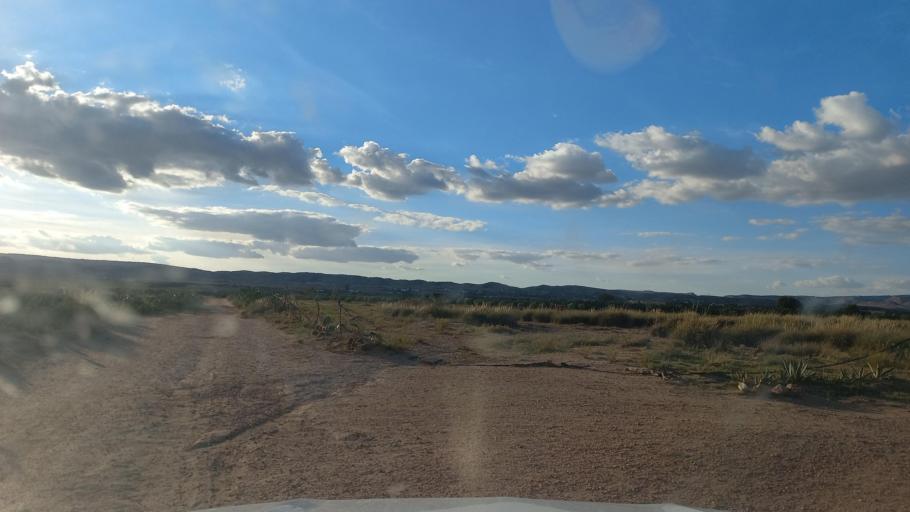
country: TN
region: Al Qasrayn
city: Sbiba
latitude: 35.3514
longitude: 9.0371
